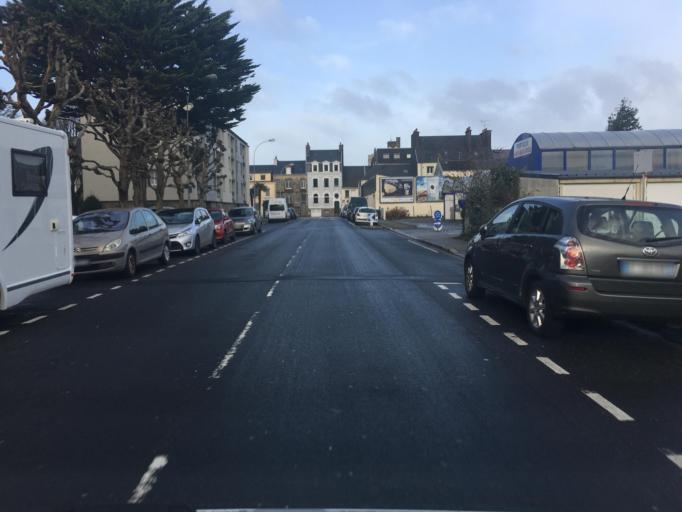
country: FR
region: Lower Normandy
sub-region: Departement de la Manche
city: Cherbourg-Octeville
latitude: 49.6380
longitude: -1.6058
